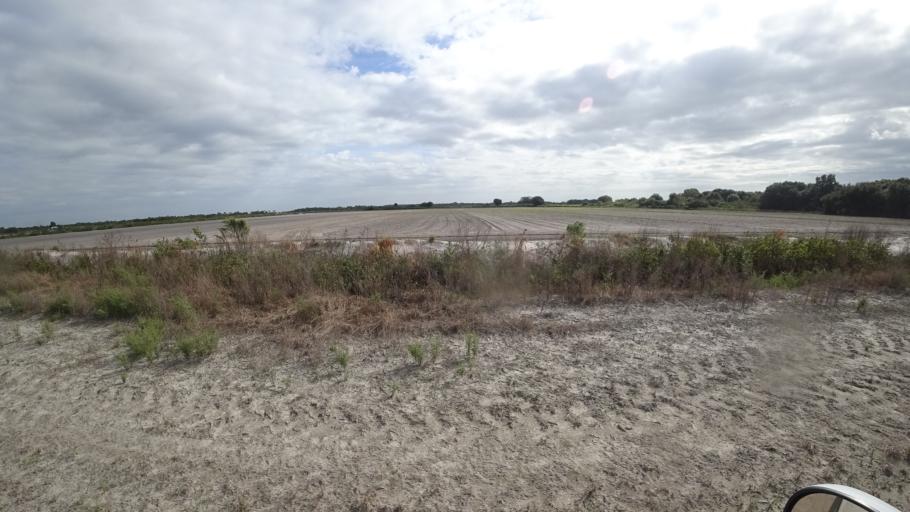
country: US
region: Florida
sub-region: Hillsborough County
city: Wimauma
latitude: 27.5596
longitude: -82.3023
